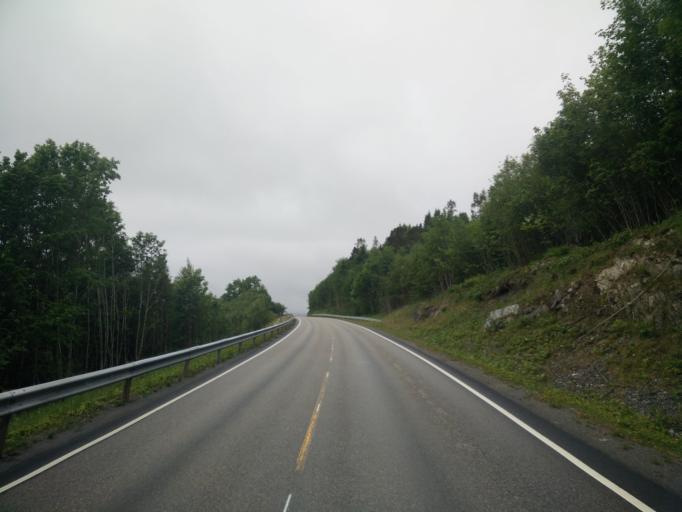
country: NO
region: More og Romsdal
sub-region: Kristiansund
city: Rensvik
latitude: 63.0036
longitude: 7.9520
